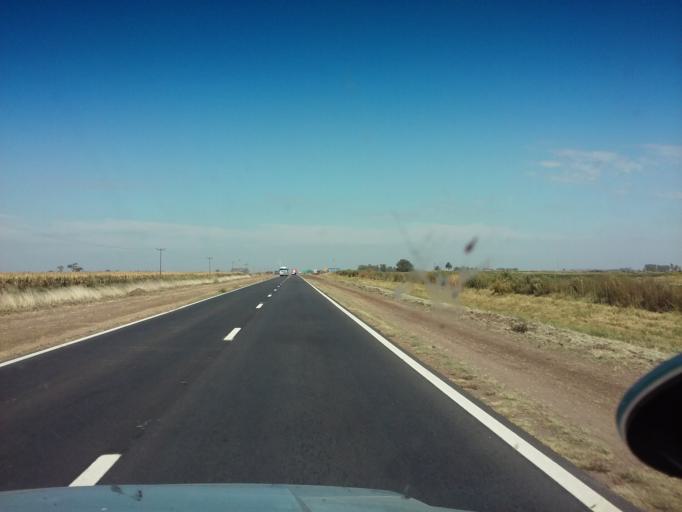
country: AR
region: Buenos Aires
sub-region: Partido de Nueve de Julio
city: Nueve de Julio
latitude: -35.3669
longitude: -60.7103
